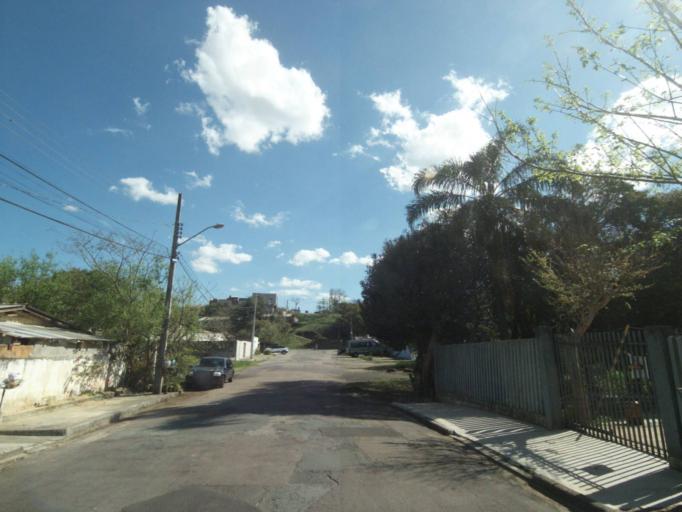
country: BR
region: Parana
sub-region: Curitiba
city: Curitiba
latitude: -25.3816
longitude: -49.2482
